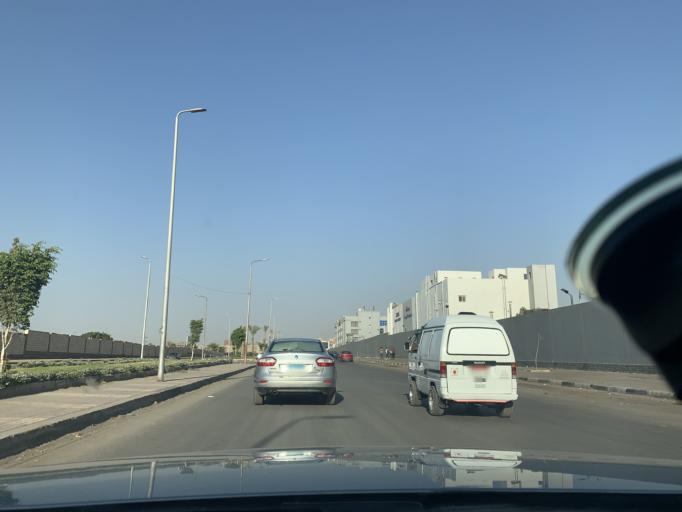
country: EG
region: Muhafazat al Qahirah
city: Cairo
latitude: 30.0351
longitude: 31.3484
